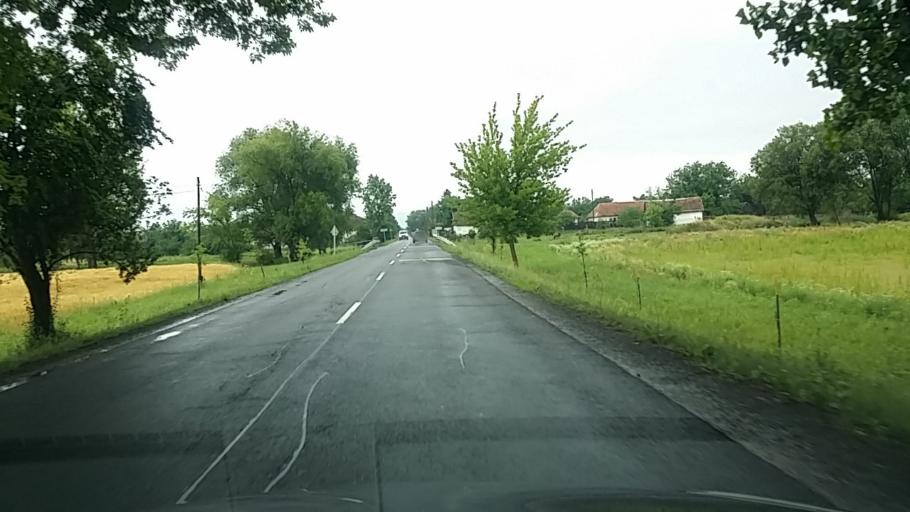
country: HU
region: Komarom-Esztergom
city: Esztergom
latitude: 47.9268
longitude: 18.7763
